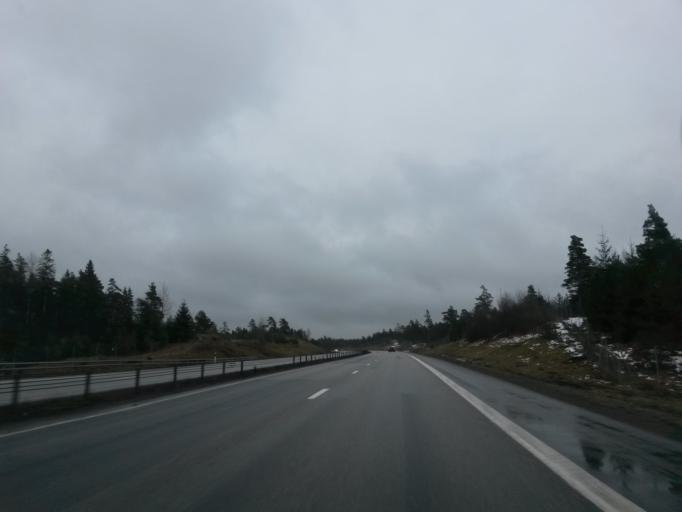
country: SE
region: Vaestra Goetaland
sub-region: Uddevalla Kommun
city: Uddevalla
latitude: 58.3303
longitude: 12.0239
